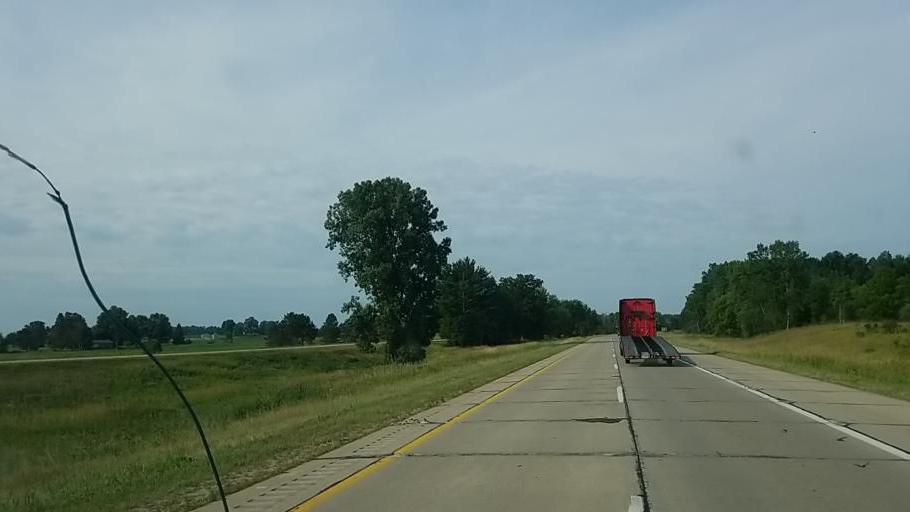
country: US
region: Michigan
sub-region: Eaton County
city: Olivet
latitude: 42.4820
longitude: -84.8785
